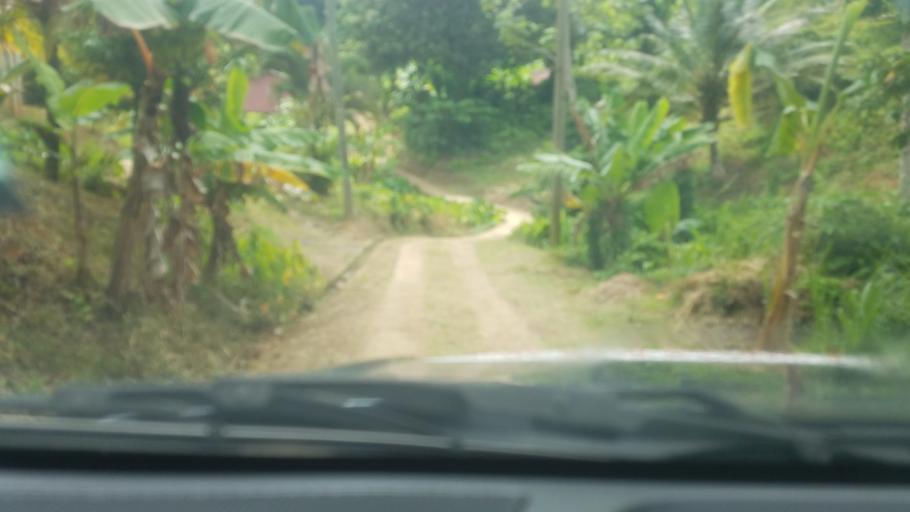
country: LC
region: Micoud Quarter
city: Micoud
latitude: 13.8043
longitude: -60.9485
